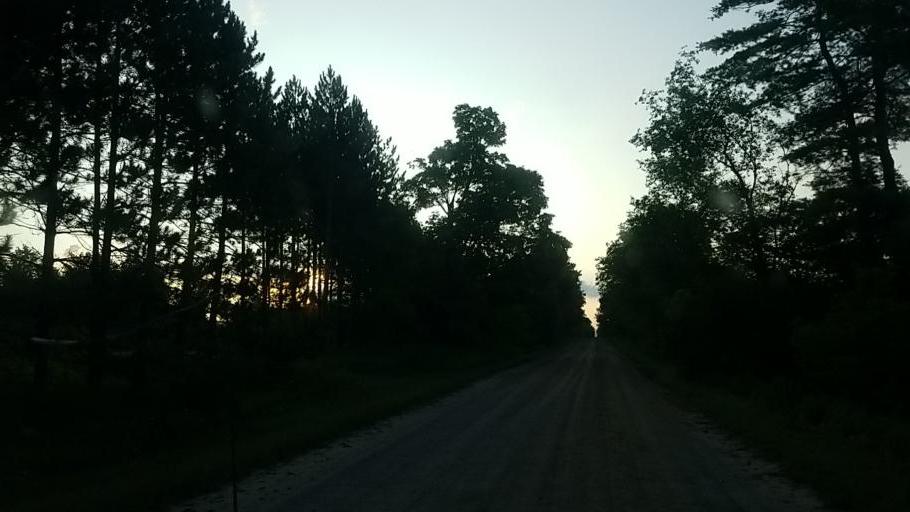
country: US
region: Michigan
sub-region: Osceola County
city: Evart
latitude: 43.9152
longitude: -85.1785
